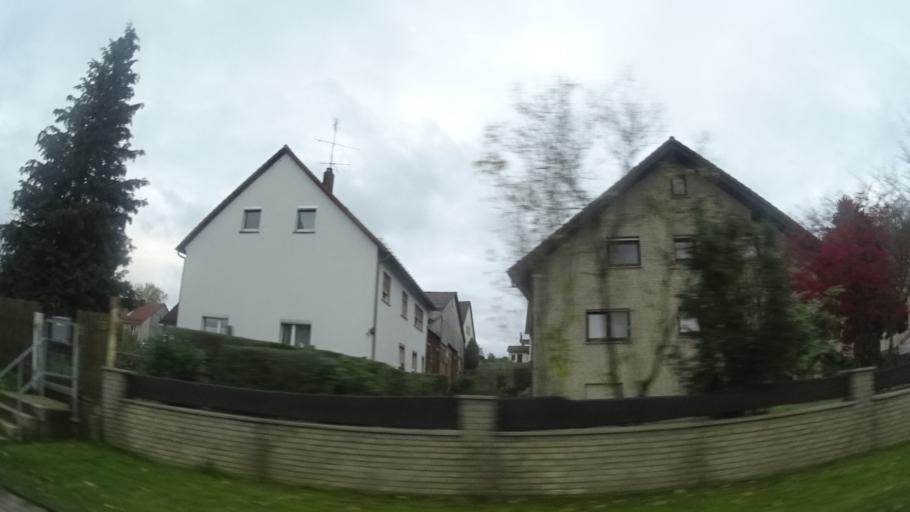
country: DE
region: Hesse
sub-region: Regierungsbezirk Giessen
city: Freiensteinau
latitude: 50.4227
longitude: 9.4090
